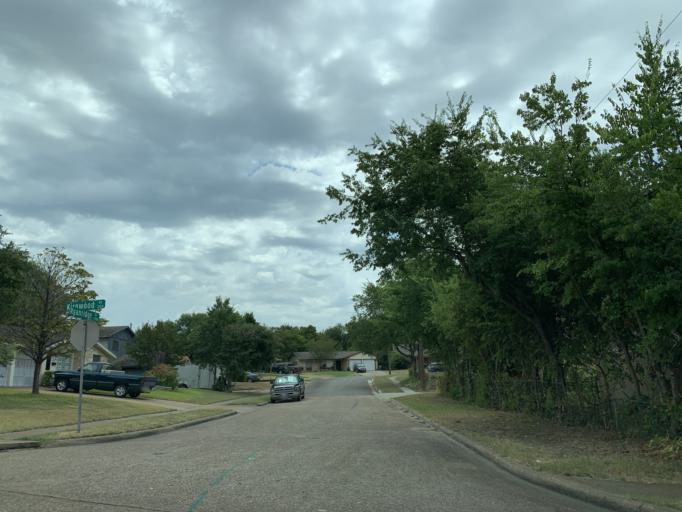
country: US
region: Texas
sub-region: Dallas County
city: DeSoto
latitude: 32.6545
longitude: -96.8253
